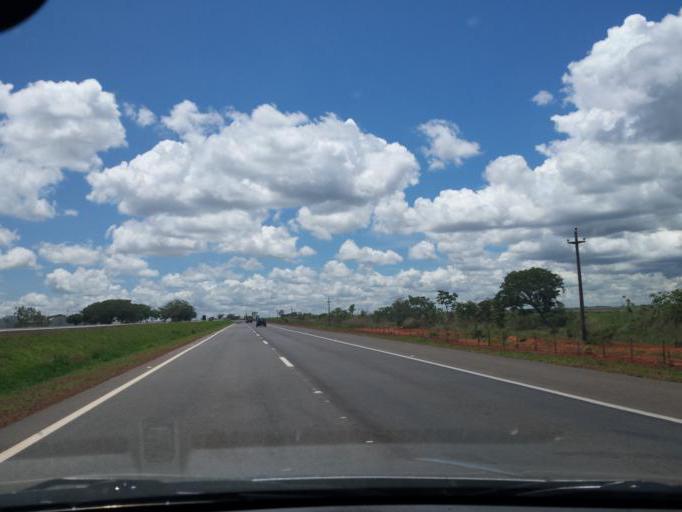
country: BR
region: Goias
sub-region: Cristalina
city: Cristalina
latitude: -16.7002
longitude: -47.6924
